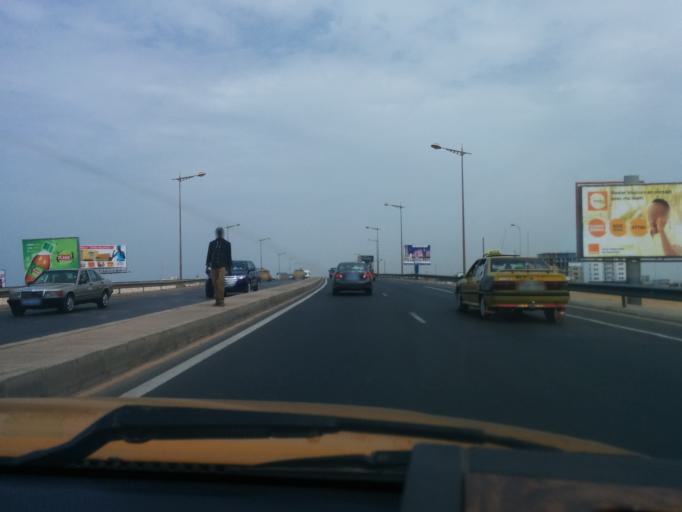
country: SN
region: Dakar
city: Grand Dakar
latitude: 14.7473
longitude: -17.4640
